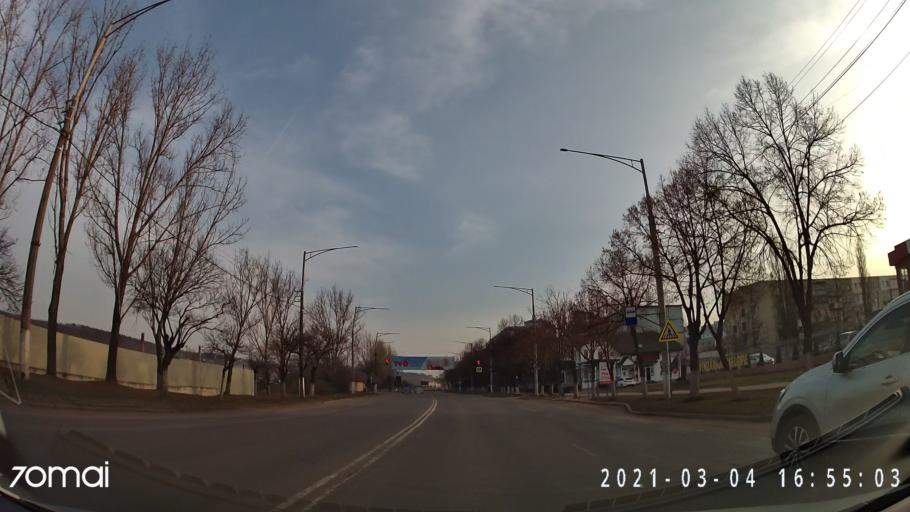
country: MD
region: Balti
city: Balti
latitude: 47.7590
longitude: 27.9408
